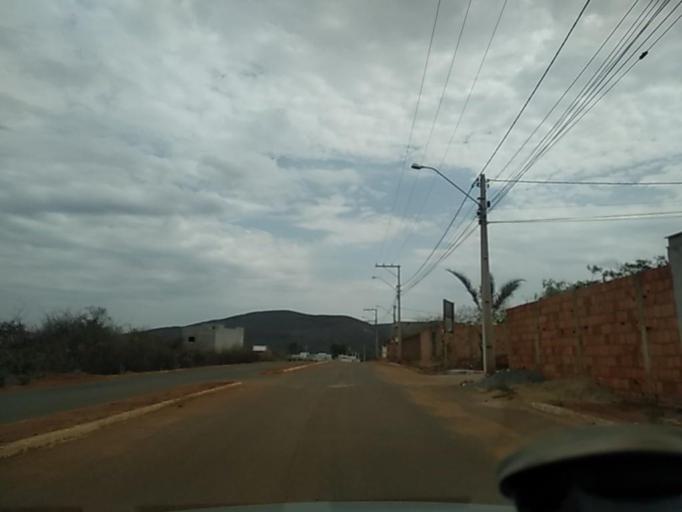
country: BR
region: Bahia
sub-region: Caetite
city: Caetite
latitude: -14.0560
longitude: -42.4718
